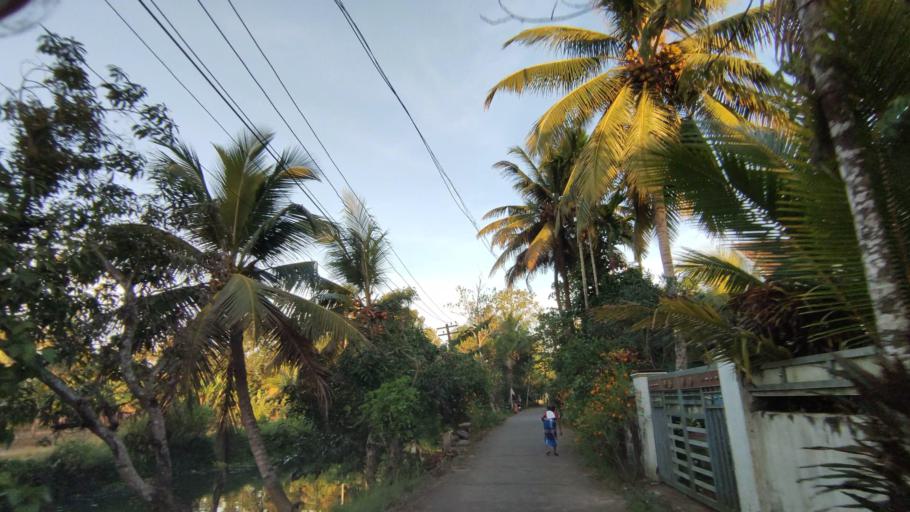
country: IN
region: Kerala
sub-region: Kottayam
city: Kottayam
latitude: 9.6321
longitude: 76.4818
